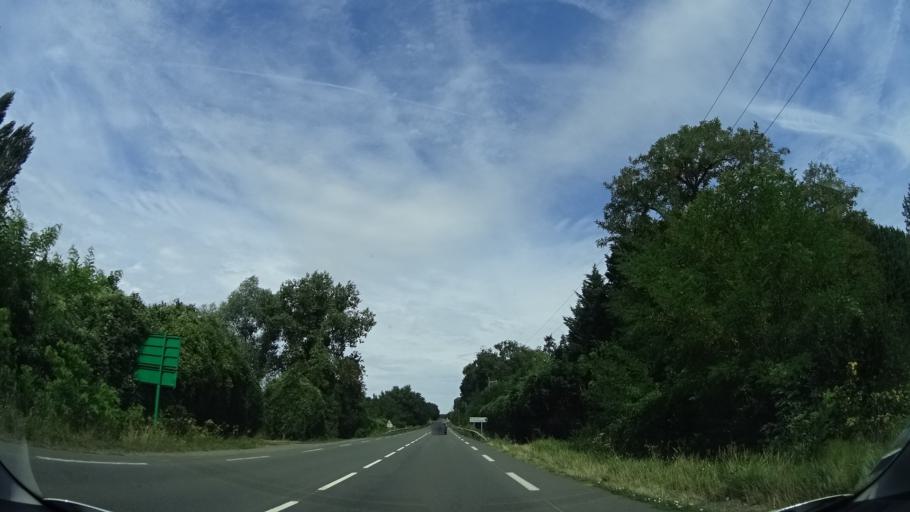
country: FR
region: Pays de la Loire
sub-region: Departement de la Sarthe
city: La Fleche
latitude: 47.7231
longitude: -0.1094
